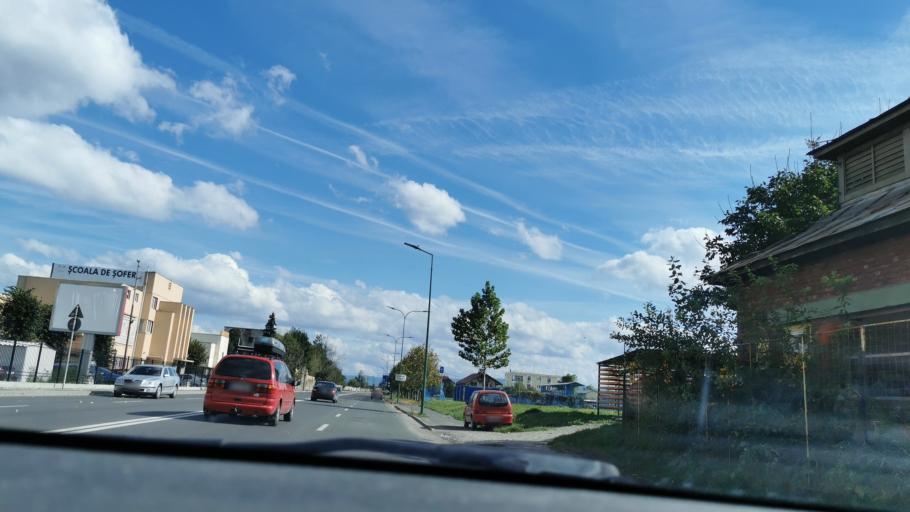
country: RO
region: Brasov
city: Brasov
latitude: 45.6489
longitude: 25.6490
